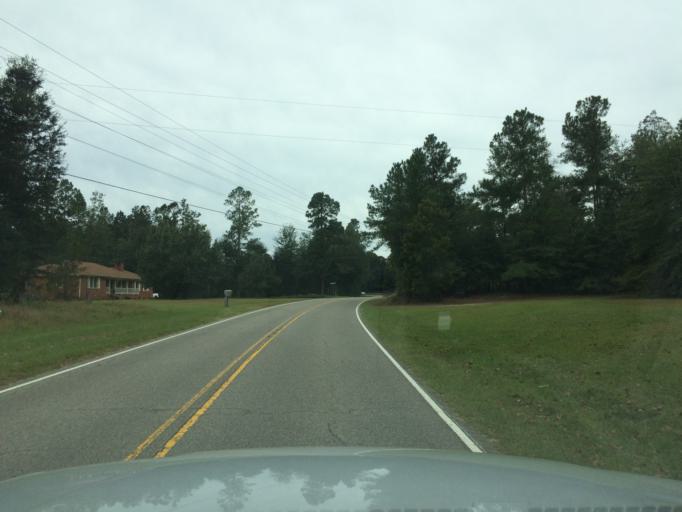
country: US
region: South Carolina
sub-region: Aiken County
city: New Ellenton
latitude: 33.4079
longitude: -81.6983
